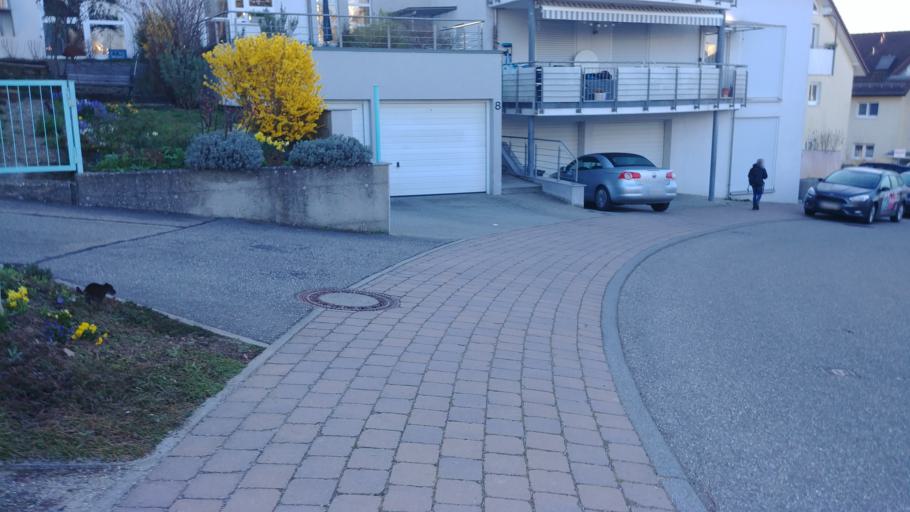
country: DE
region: Baden-Wuerttemberg
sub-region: Regierungsbezirk Stuttgart
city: Untereisesheim
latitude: 49.1977
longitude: 9.1954
